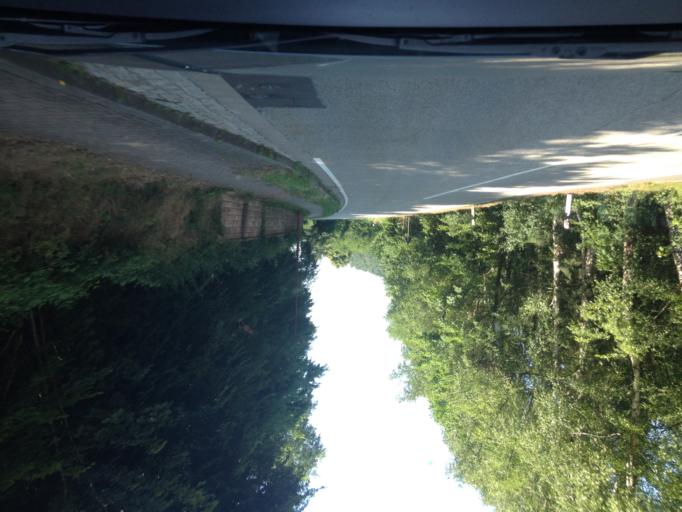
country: DE
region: Rheinland-Pfalz
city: Frankenstein
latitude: 49.4406
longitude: 7.9845
